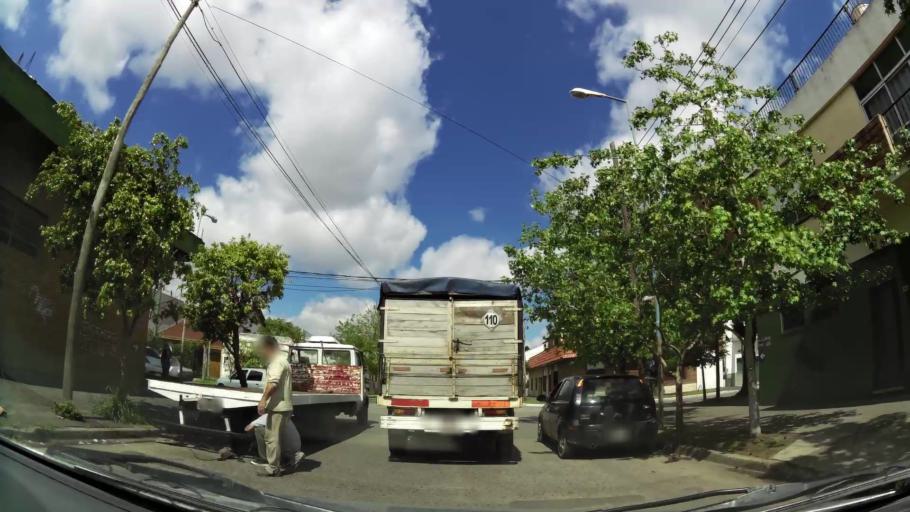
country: AR
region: Buenos Aires
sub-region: Partido de Lanus
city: Lanus
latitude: -34.6884
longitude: -58.4188
